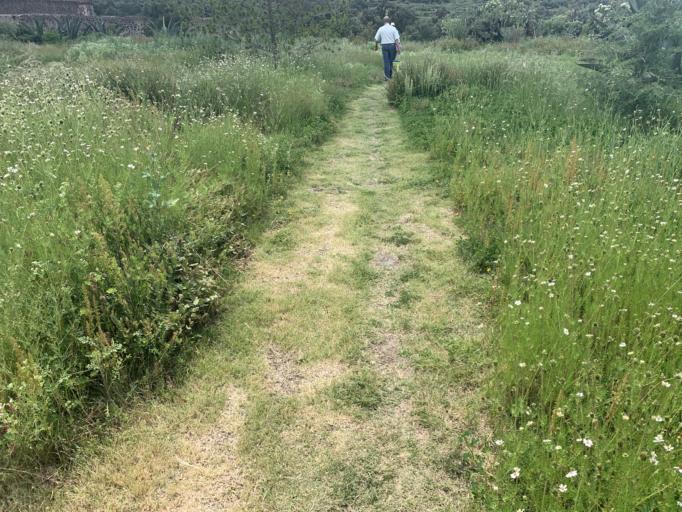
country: MX
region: Hidalgo
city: Zempoala
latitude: 19.9352
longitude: -98.5983
